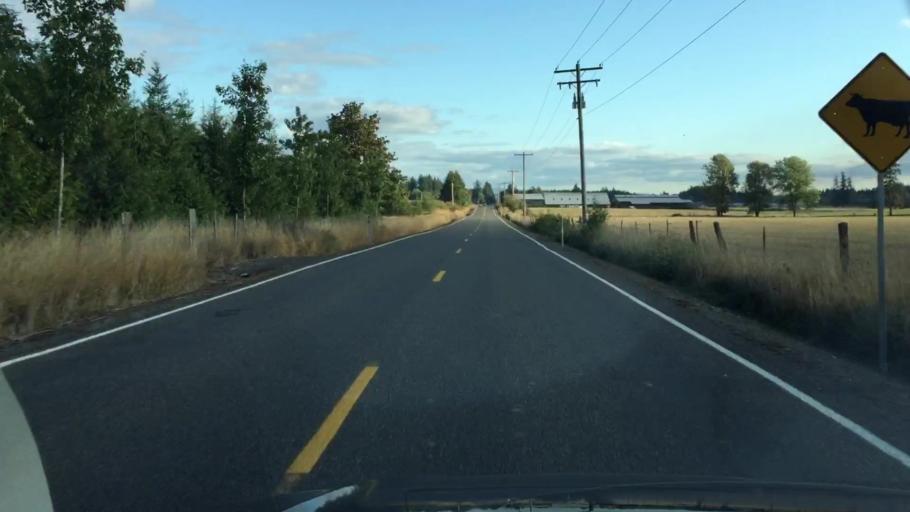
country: US
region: Washington
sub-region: Lewis County
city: Napavine
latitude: 46.5275
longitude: -122.7405
